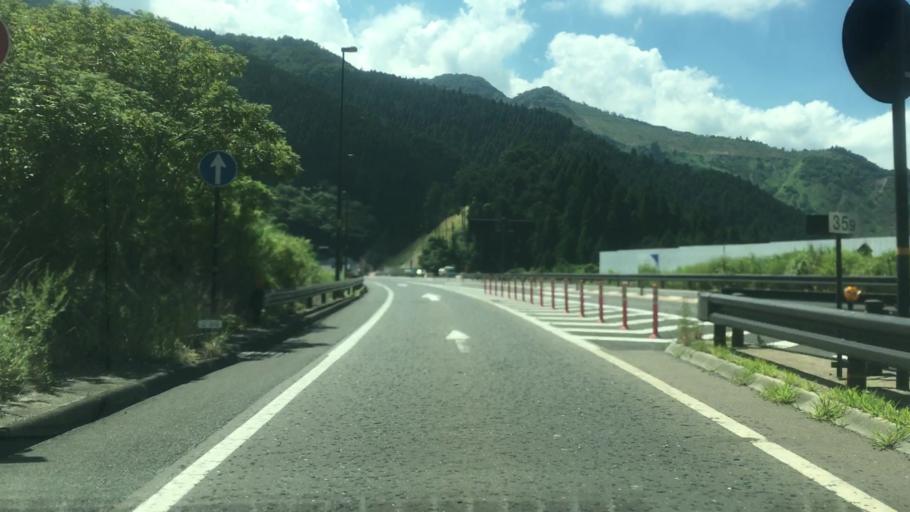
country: JP
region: Tottori
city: Tottori
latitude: 35.2852
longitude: 134.2246
